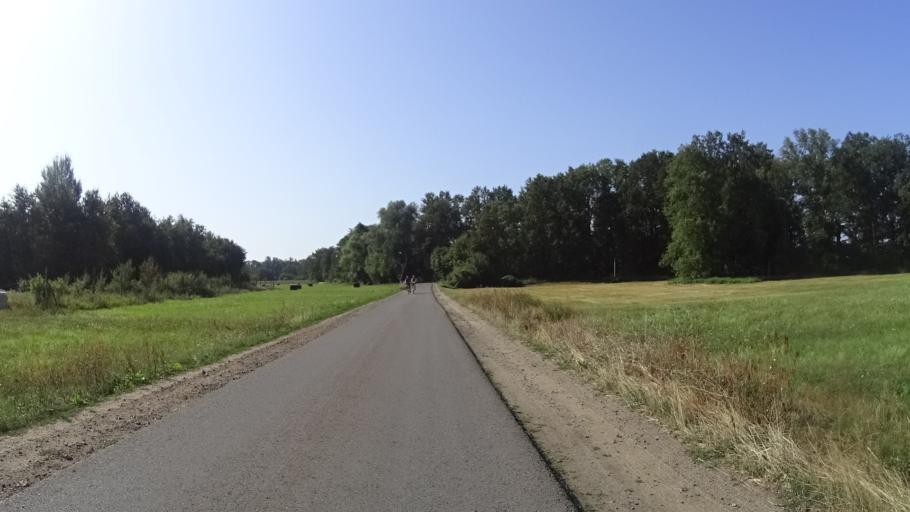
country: DE
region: Brandenburg
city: Straupitz
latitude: 51.8812
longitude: 14.1203
